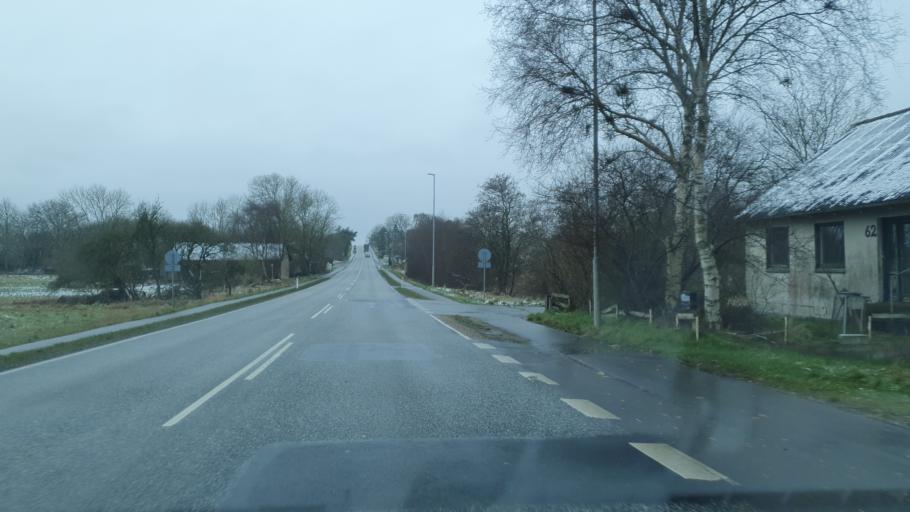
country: DK
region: North Denmark
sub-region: Jammerbugt Kommune
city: Brovst
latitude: 57.0951
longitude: 9.4809
